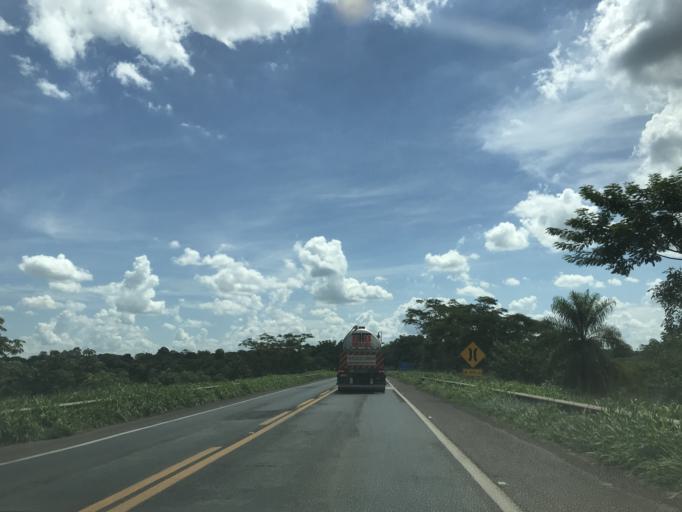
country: BR
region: Sao Paulo
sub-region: Nova Granada
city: Nova Granada
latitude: -20.4174
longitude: -49.2647
